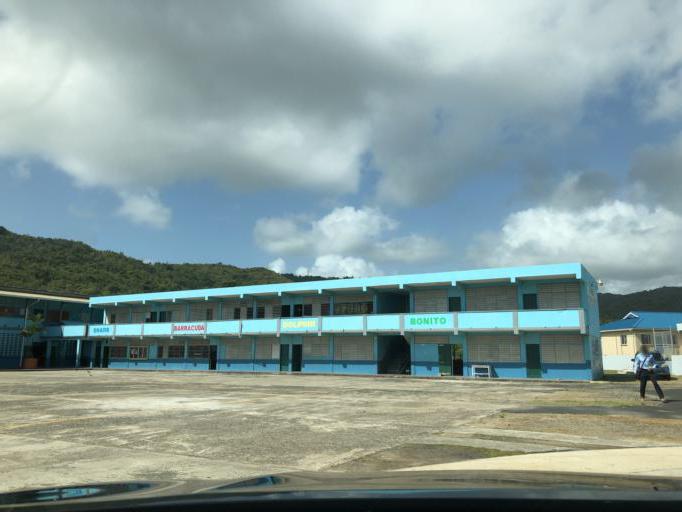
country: LC
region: Dennery Quarter
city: Dennery
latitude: 13.9103
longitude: -60.8934
